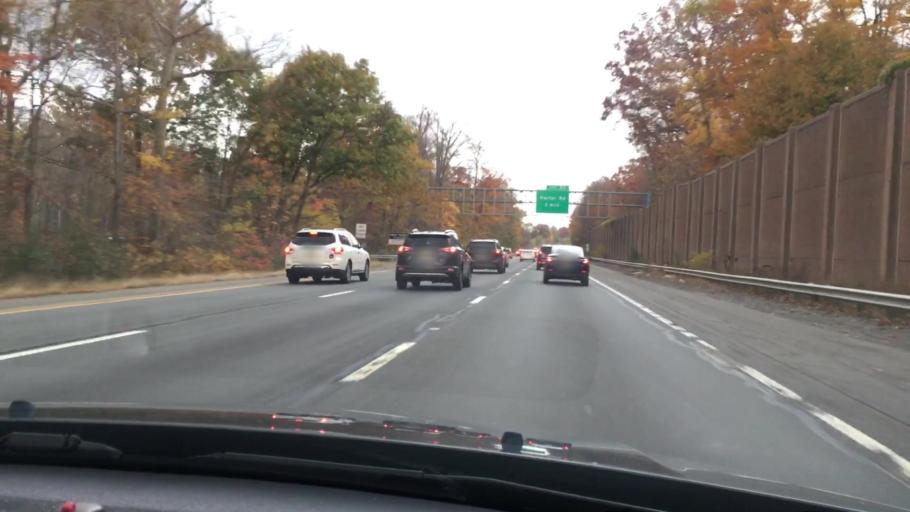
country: US
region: New Jersey
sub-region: Morris County
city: Morristown
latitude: 40.7793
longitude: -74.4750
